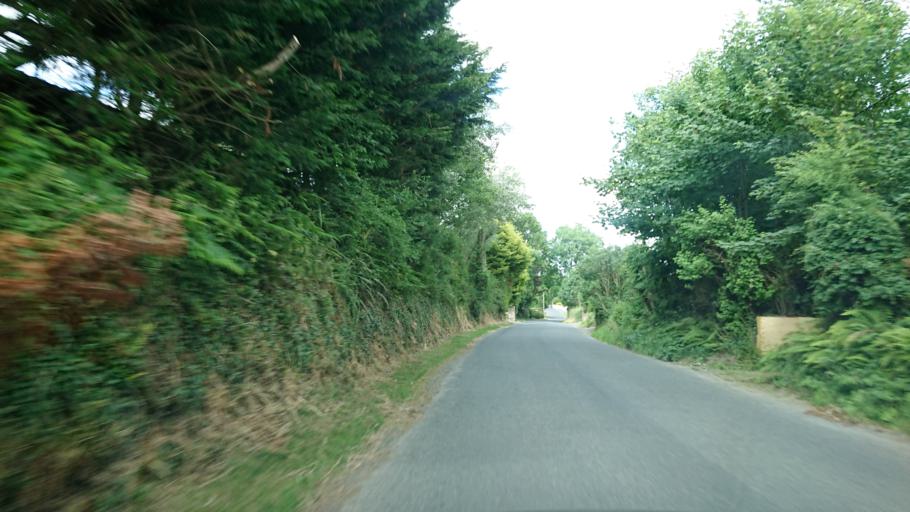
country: IE
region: Munster
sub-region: Waterford
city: Waterford
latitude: 52.2244
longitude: -7.1516
